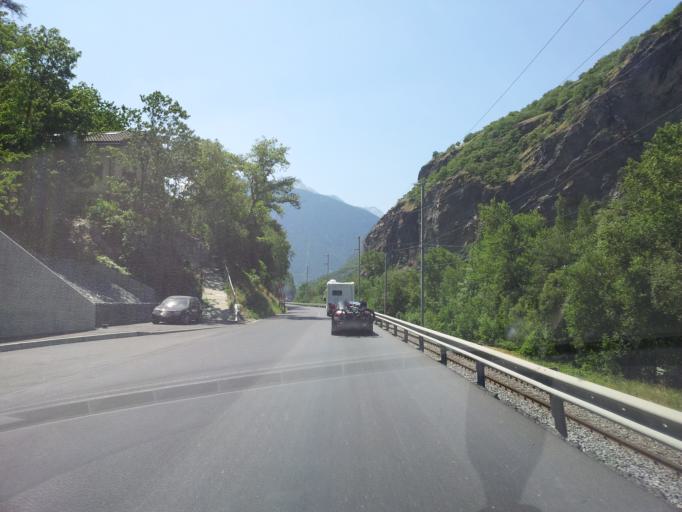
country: CH
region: Valais
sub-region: Visp District
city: Visp
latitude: 46.2758
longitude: 7.8824
